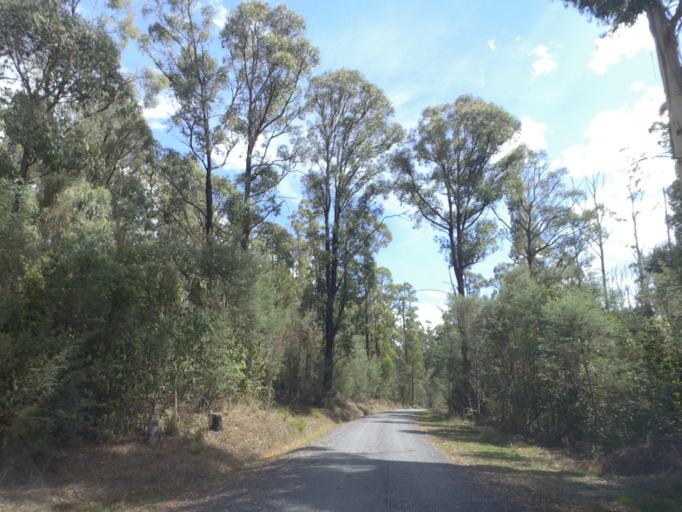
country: AU
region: Victoria
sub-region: Murrindindi
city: Alexandra
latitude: -37.4486
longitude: 145.7547
